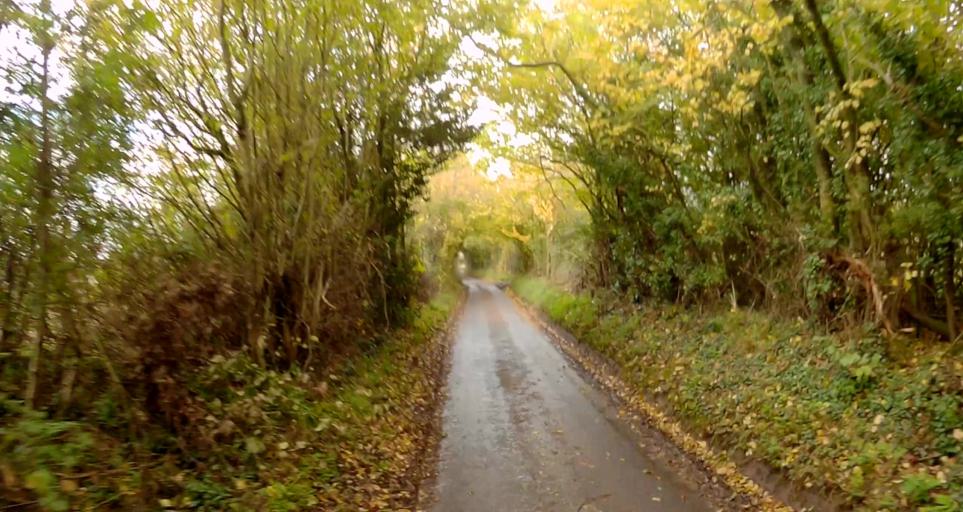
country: GB
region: England
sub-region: Hampshire
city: Long Sutton
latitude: 51.2123
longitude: -0.9437
